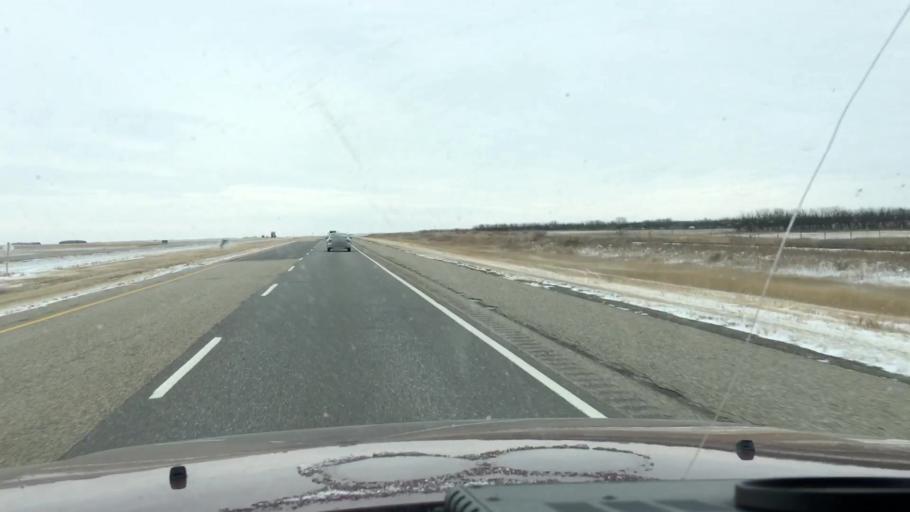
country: CA
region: Saskatchewan
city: Saskatoon
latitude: 51.4687
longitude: -106.2448
